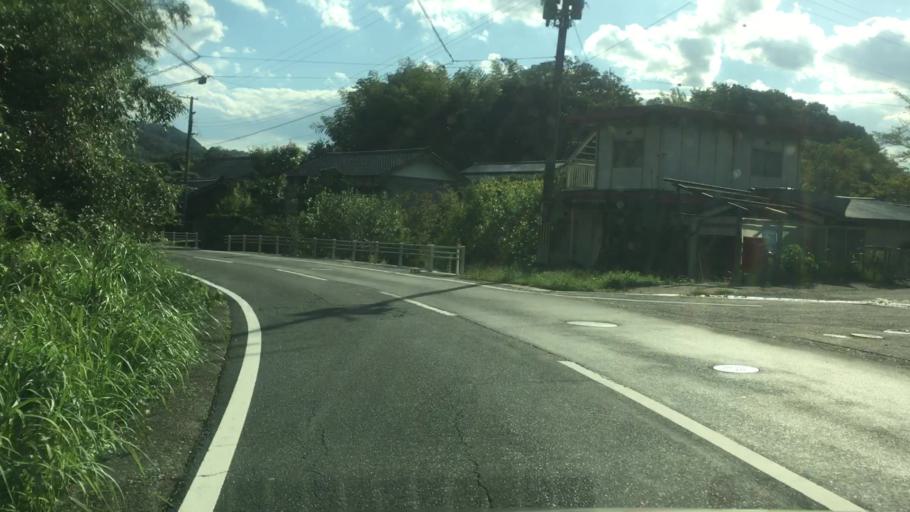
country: JP
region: Hyogo
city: Toyooka
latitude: 35.6381
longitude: 134.9423
